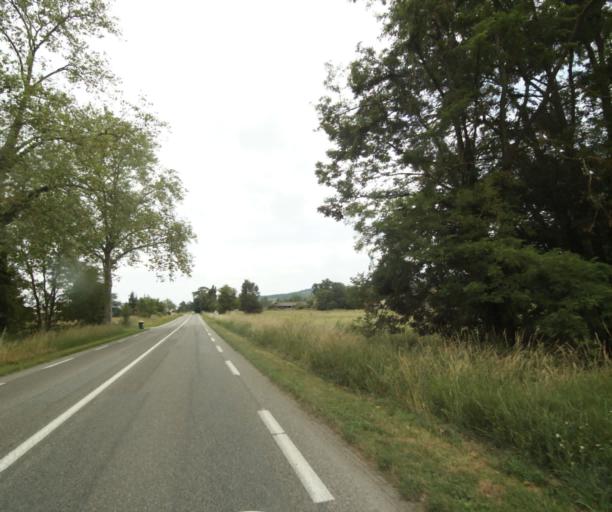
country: FR
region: Midi-Pyrenees
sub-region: Departement du Tarn-et-Garonne
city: Saint-Nauphary
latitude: 43.9711
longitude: 1.4205
